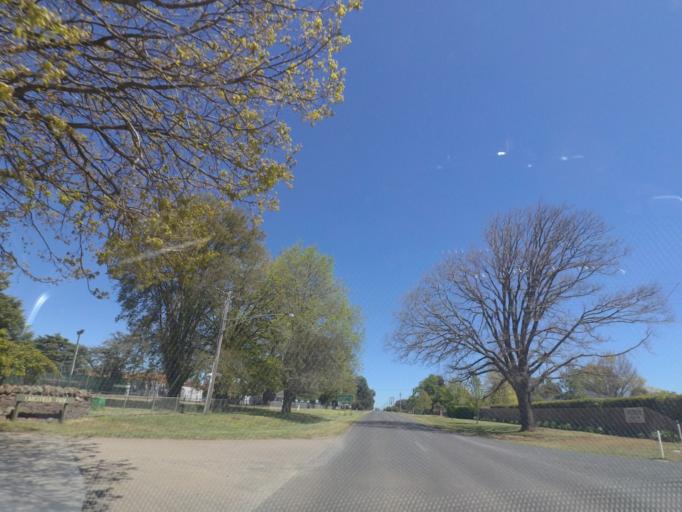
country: AU
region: Victoria
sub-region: Hume
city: Sunbury
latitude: -37.2792
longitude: 144.7243
